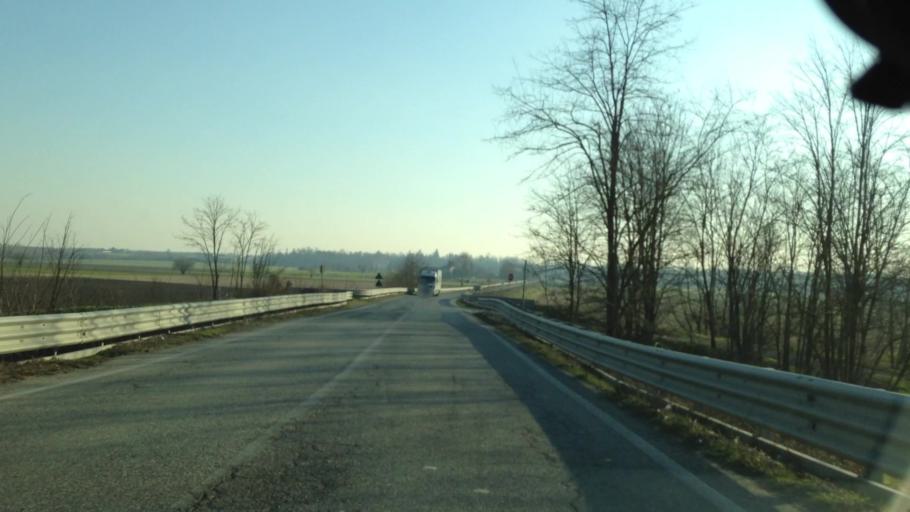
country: IT
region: Piedmont
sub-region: Provincia di Alessandria
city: Felizzano
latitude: 44.8892
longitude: 8.4397
